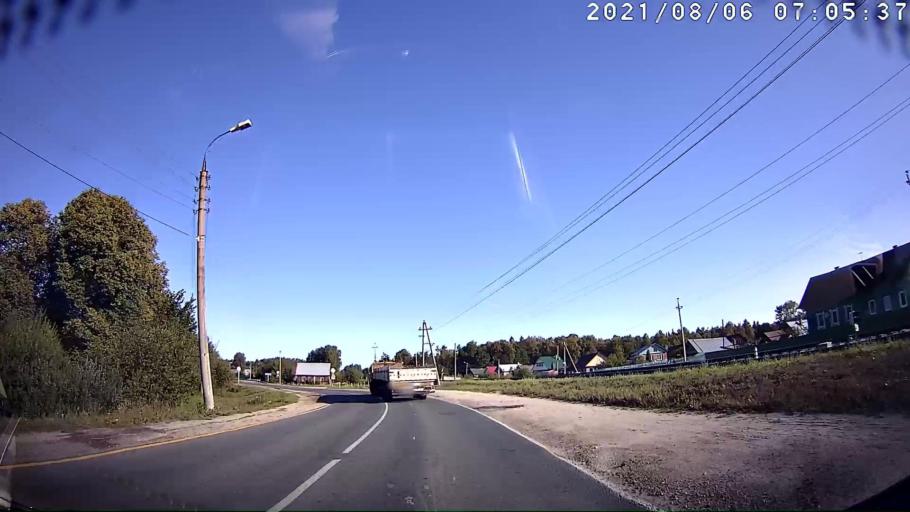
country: RU
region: Mariy-El
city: Yoshkar-Ola
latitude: 56.5546
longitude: 47.9862
